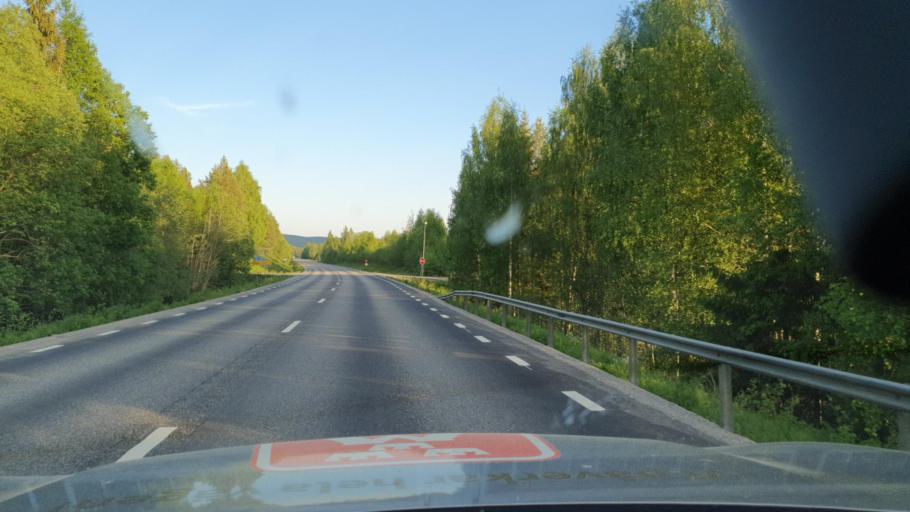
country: SE
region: Vaesternorrland
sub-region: Solleftea Kommun
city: As
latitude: 63.5831
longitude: 16.8230
